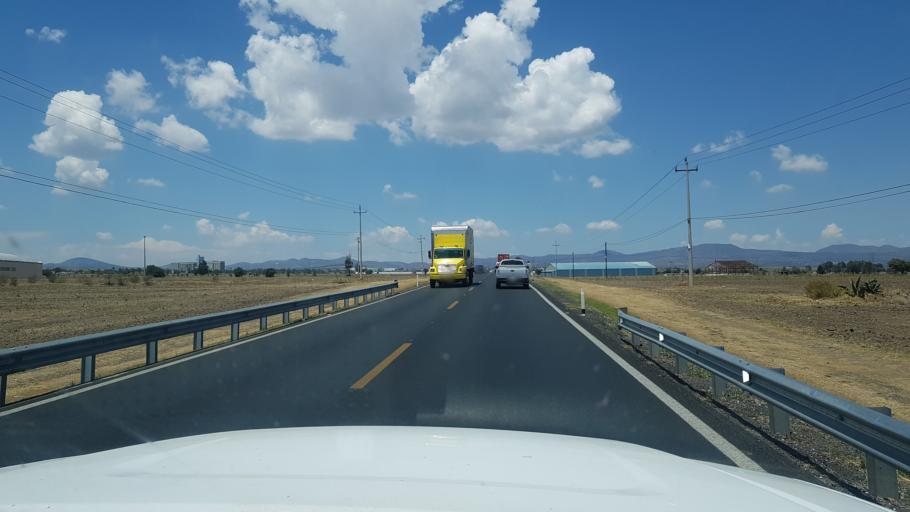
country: MX
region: Hidalgo
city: Calpulalpan
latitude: 19.5787
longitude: -98.5236
